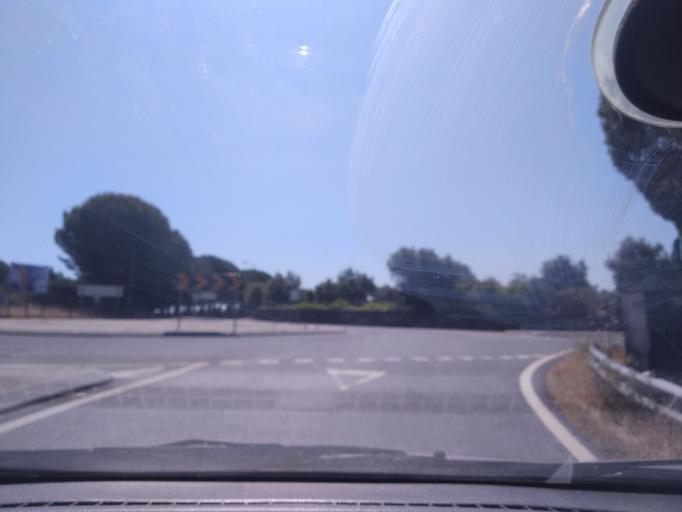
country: PT
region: Guarda
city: Alcains
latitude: 39.9175
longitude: -7.4711
